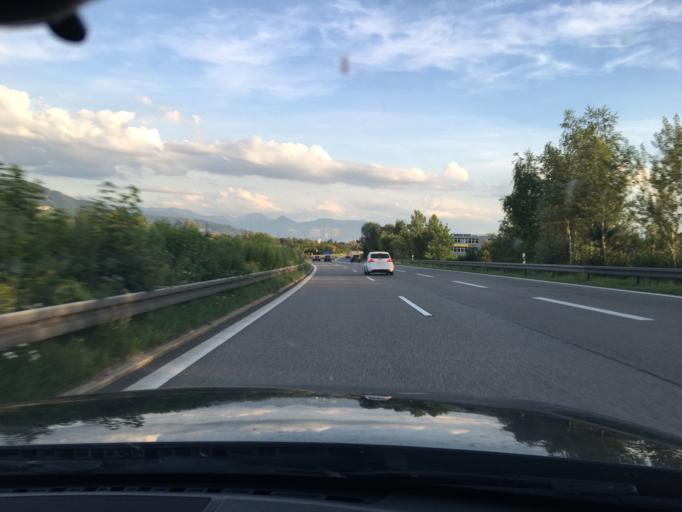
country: AT
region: Vorarlberg
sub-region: Politischer Bezirk Bregenz
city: Horbranz
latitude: 47.5528
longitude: 9.7335
